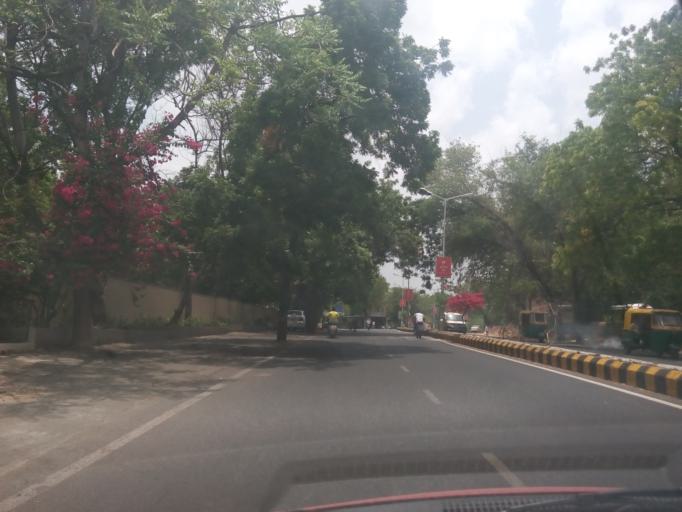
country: IN
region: Gujarat
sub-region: Ahmadabad
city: Sarkhej
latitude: 23.0441
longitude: 72.5189
